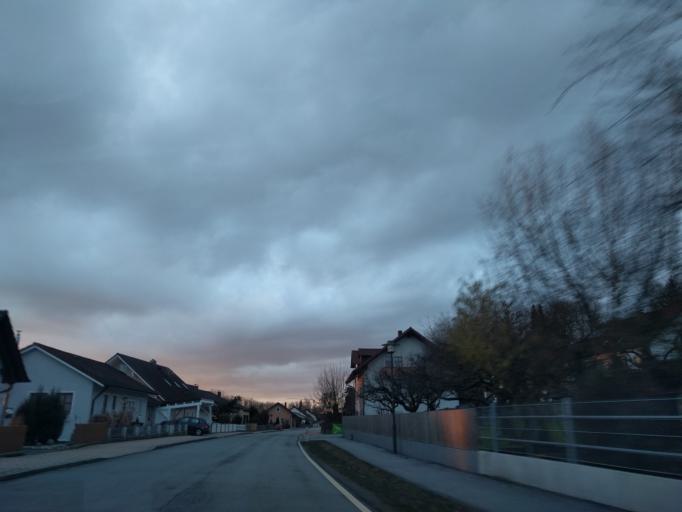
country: DE
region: Bavaria
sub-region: Lower Bavaria
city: Winzer
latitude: 48.7198
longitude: 13.0831
